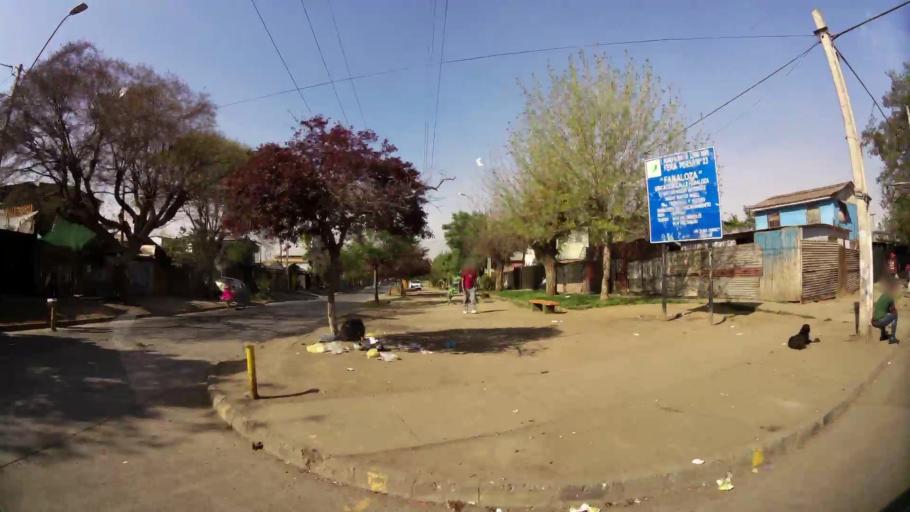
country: CL
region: Santiago Metropolitan
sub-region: Provincia de Santiago
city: Lo Prado
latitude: -33.4171
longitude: -70.7330
